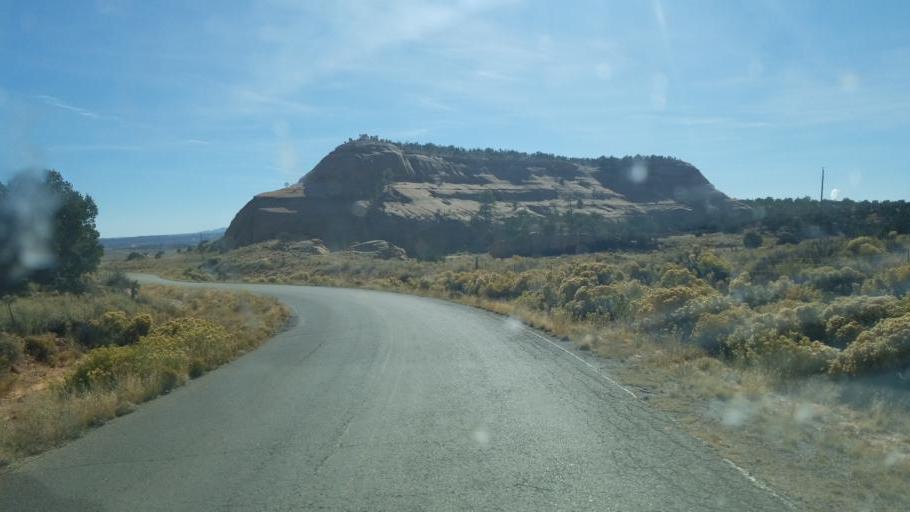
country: US
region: New Mexico
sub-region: McKinley County
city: Thoreau
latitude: 35.4354
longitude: -108.0511
